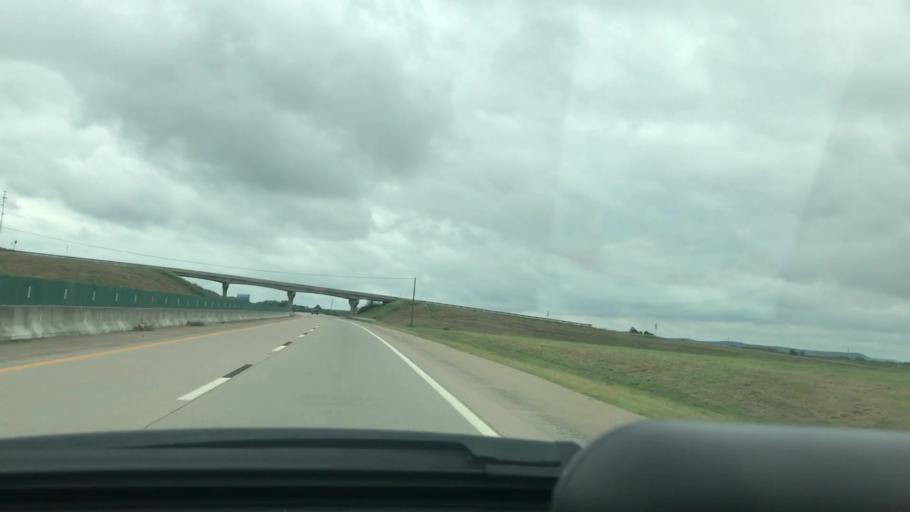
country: US
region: Oklahoma
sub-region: Pittsburg County
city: Krebs
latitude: 35.0562
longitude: -95.7071
